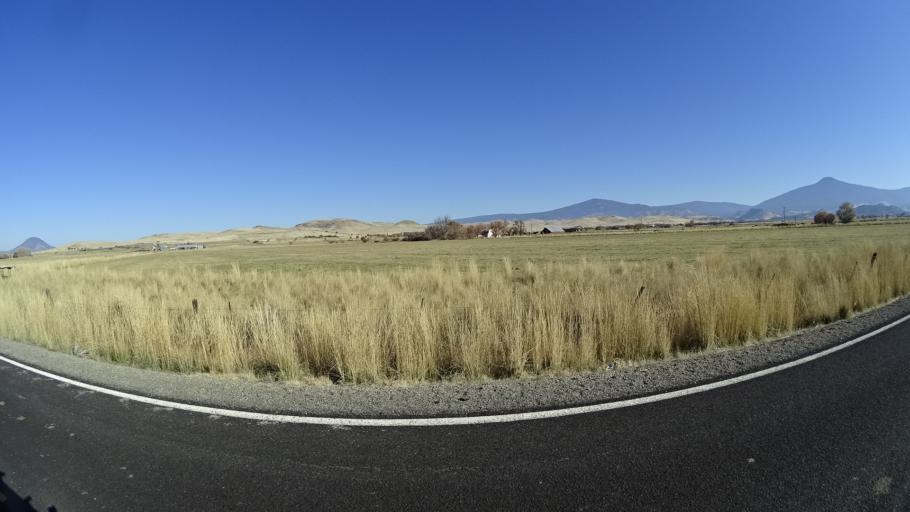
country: US
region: California
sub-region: Siskiyou County
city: Montague
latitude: 41.7136
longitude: -122.4406
